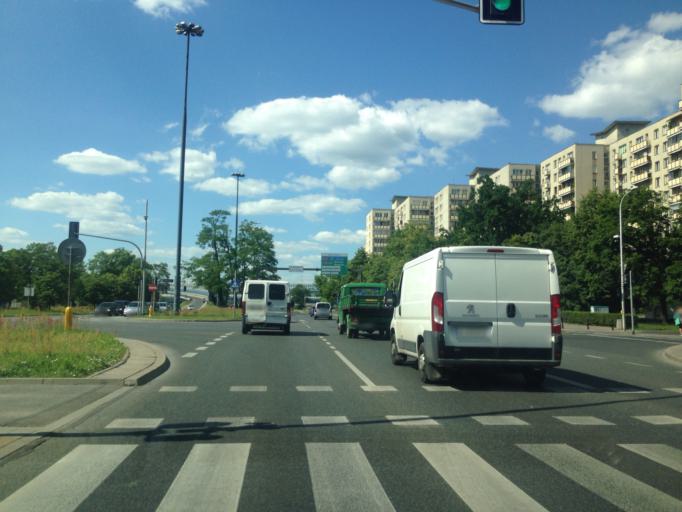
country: PL
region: Masovian Voivodeship
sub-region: Warszawa
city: Targowek
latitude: 52.2910
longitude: 21.0187
